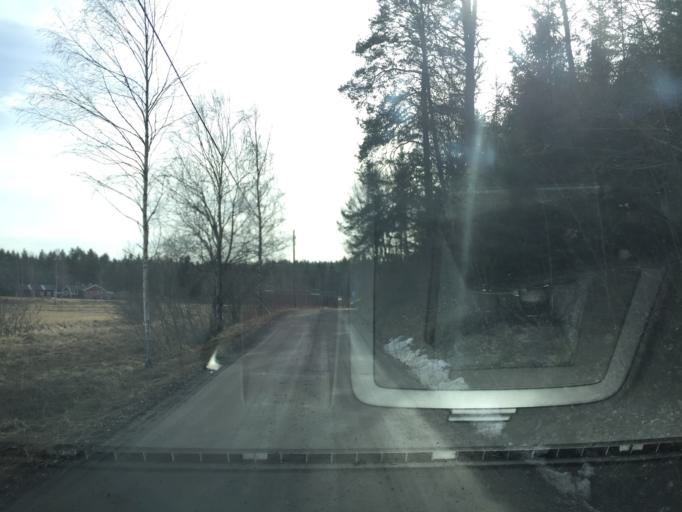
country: SE
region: Stockholm
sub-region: Botkyrka Kommun
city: Tullinge
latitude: 59.0987
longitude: 17.9682
